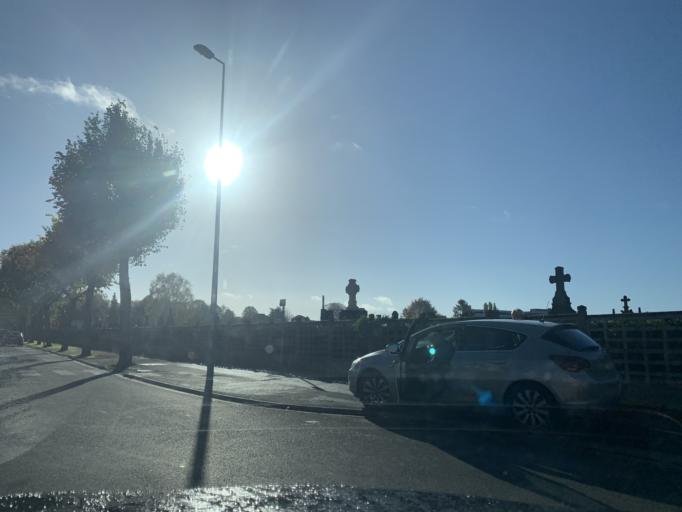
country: FR
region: Nord-Pas-de-Calais
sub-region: Departement du Nord
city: Cambrai
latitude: 50.1698
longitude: 3.2262
